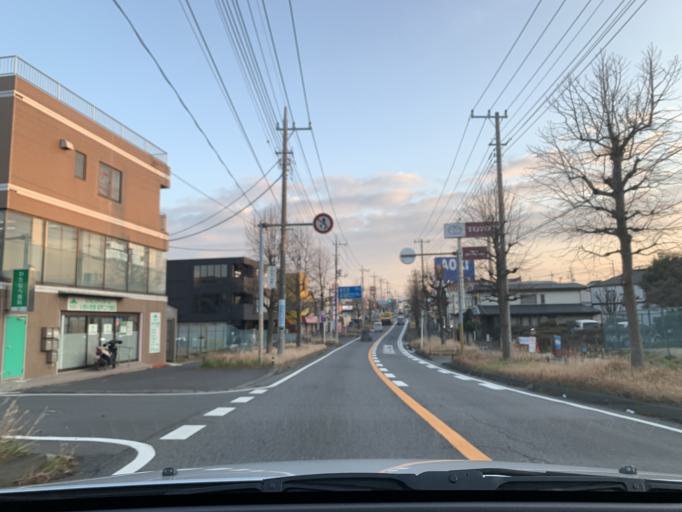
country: JP
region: Chiba
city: Matsudo
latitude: 35.7690
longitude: 139.9102
